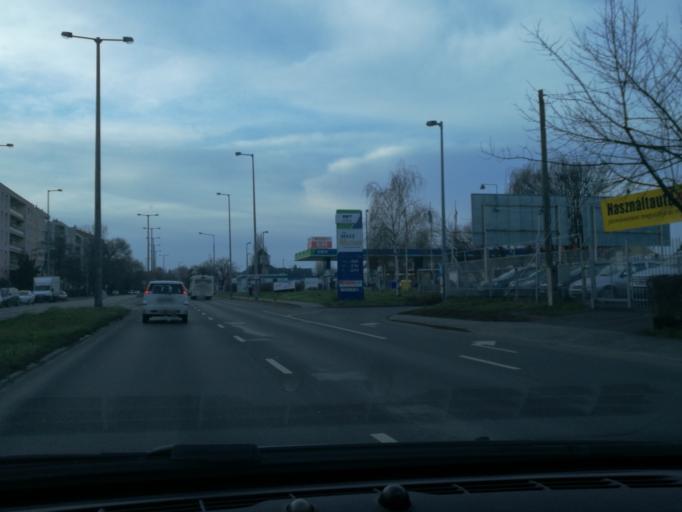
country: HU
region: Szabolcs-Szatmar-Bereg
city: Nyiregyhaza
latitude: 47.9468
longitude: 21.7260
